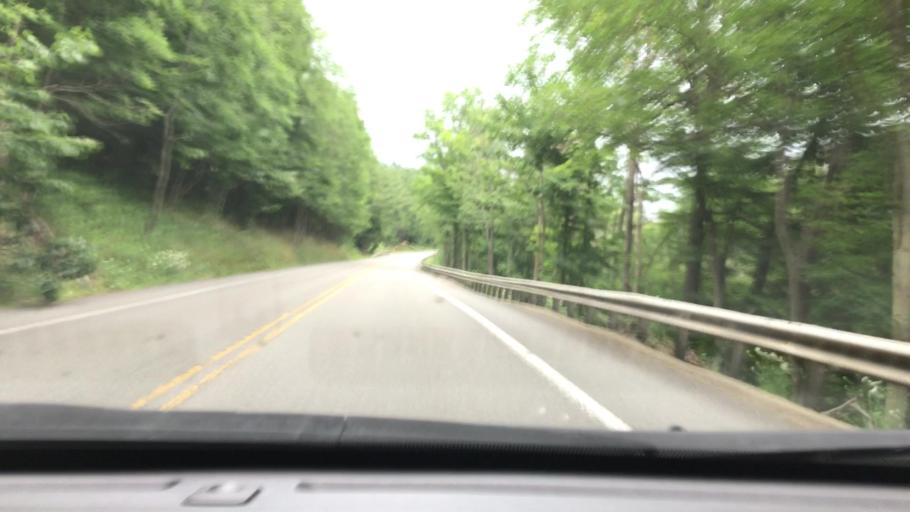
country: US
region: Pennsylvania
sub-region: McKean County
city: Bradford
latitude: 41.8575
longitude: -78.6733
